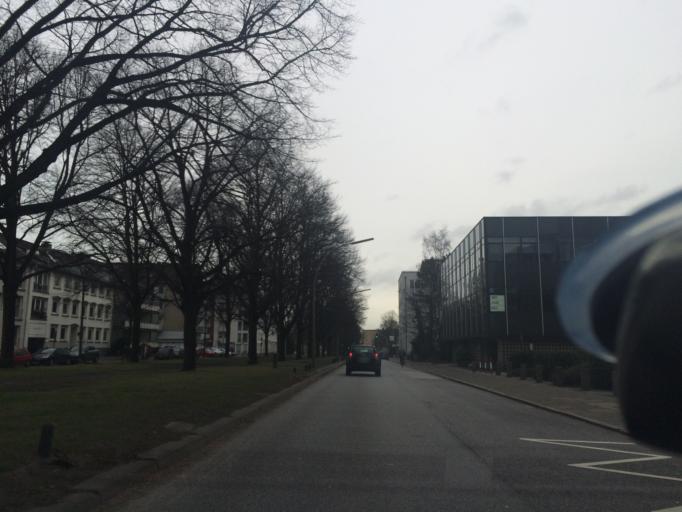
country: DE
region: Hamburg
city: Altona
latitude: 53.5462
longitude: 9.9400
